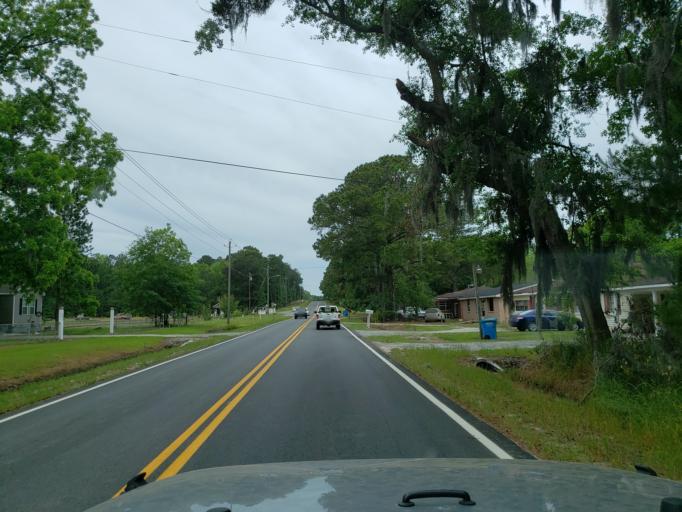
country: US
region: Georgia
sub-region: Chatham County
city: Port Wentworth
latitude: 32.1801
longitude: -81.1992
